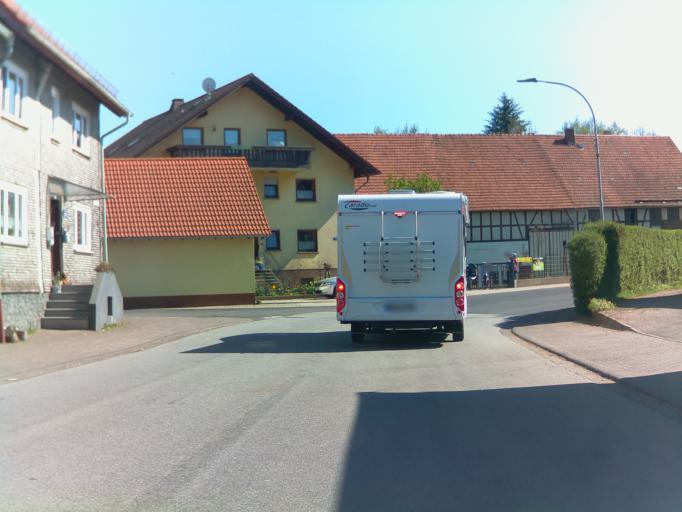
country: DE
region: Hesse
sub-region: Regierungsbezirk Giessen
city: Grebenhain
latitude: 50.5235
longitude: 9.3340
